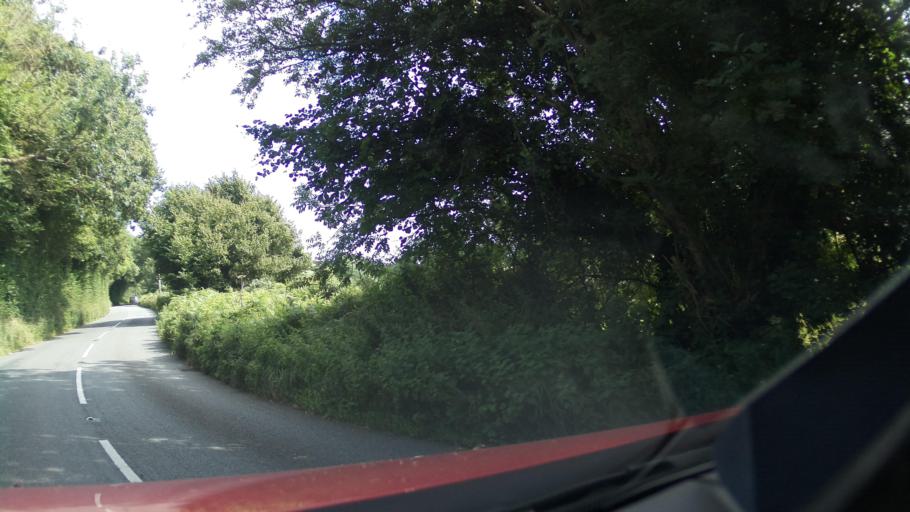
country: GB
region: England
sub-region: Devon
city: Dartmouth
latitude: 50.3621
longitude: -3.5617
